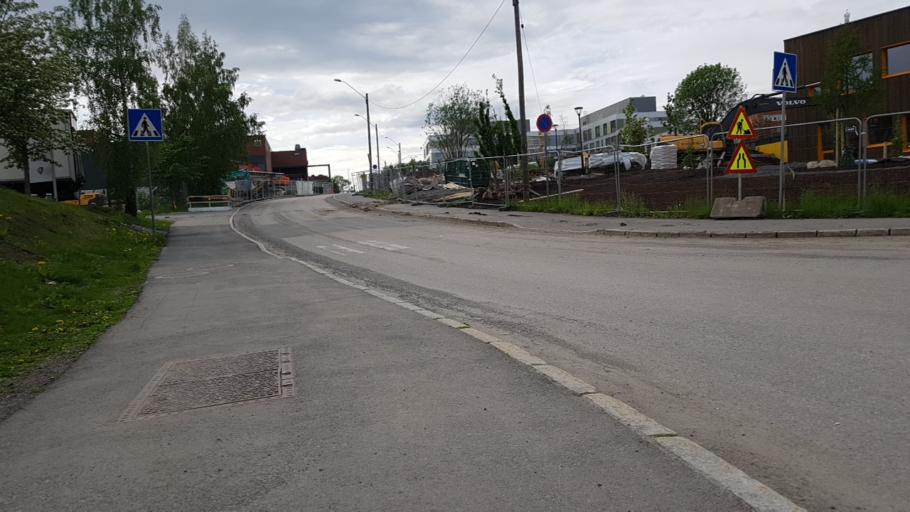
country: NO
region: Oslo
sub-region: Oslo
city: Oslo
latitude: 59.9371
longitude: 10.8301
